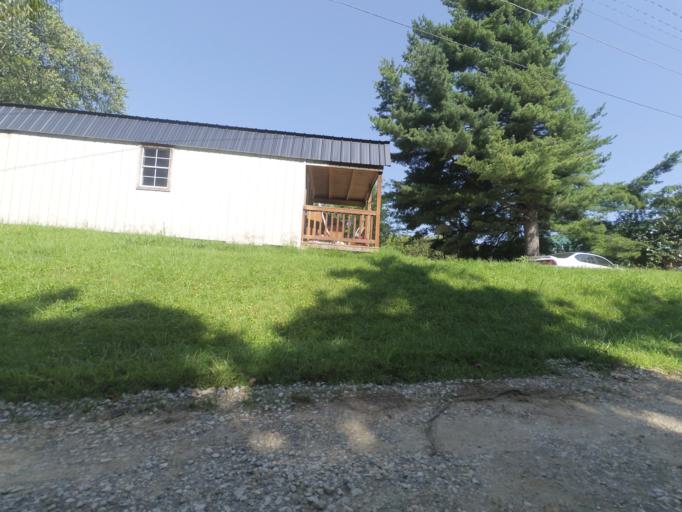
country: US
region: West Virginia
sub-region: Cabell County
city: Huntington
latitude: 38.4357
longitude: -82.4392
